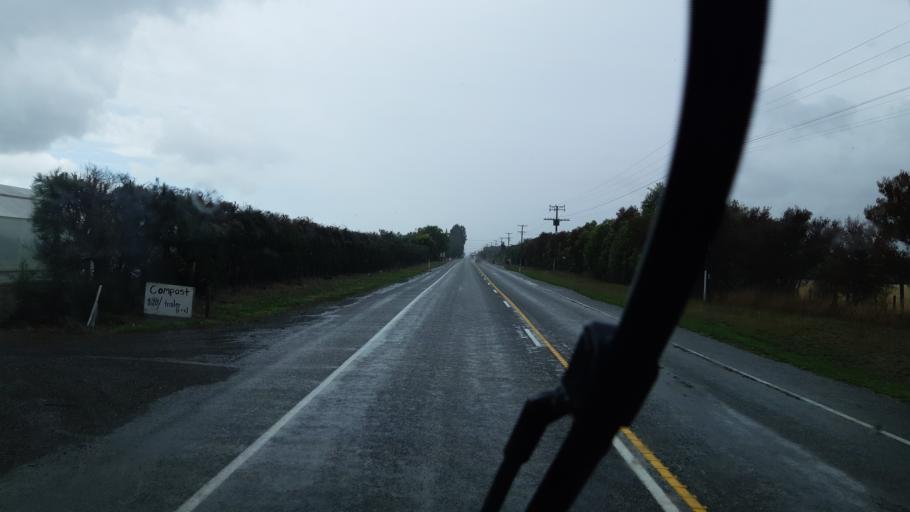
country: NZ
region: Tasman
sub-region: Tasman District
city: Brightwater
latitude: -41.3700
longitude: 173.1285
